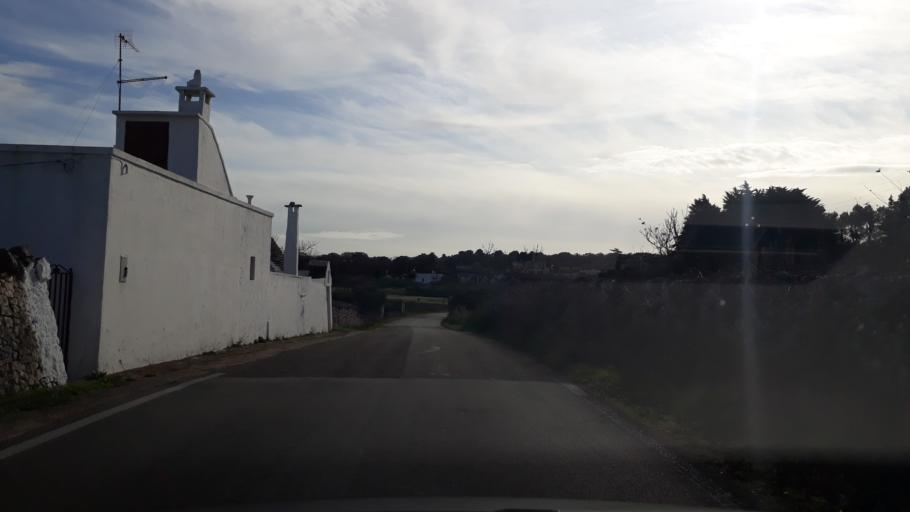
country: IT
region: Apulia
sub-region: Provincia di Taranto
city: Martina Franca
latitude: 40.6807
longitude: 17.3552
